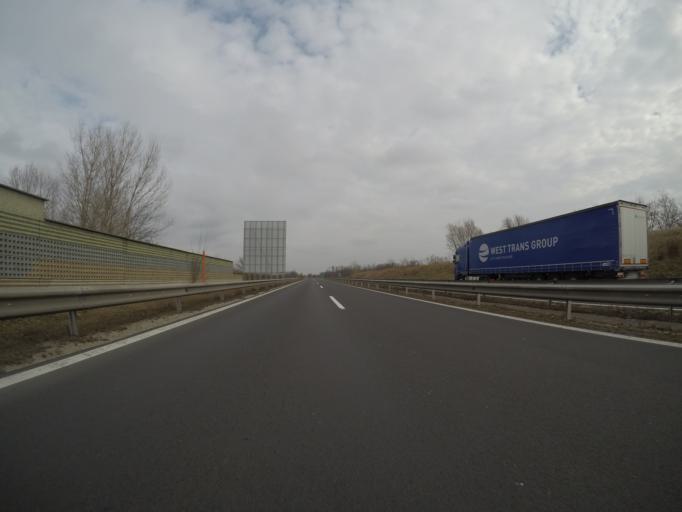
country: SI
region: Murska Sobota
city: Rakican
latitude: 46.6349
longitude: 16.1862
